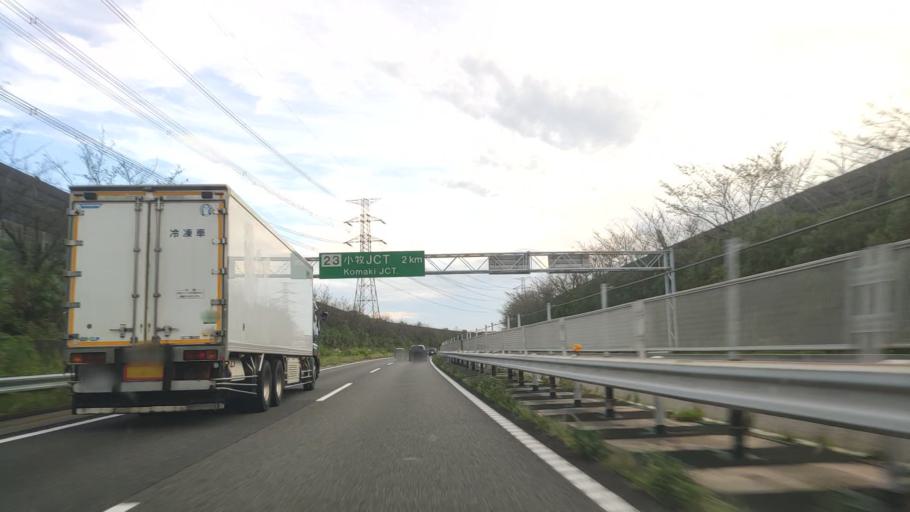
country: JP
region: Aichi
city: Kasugai
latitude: 35.3015
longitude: 136.9949
